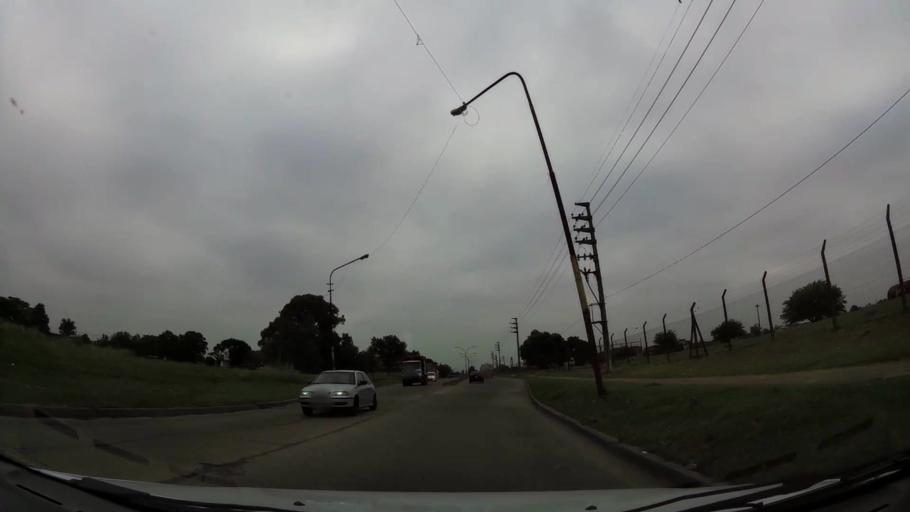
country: AR
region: Buenos Aires
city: San Justo
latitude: -34.7054
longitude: -58.5476
